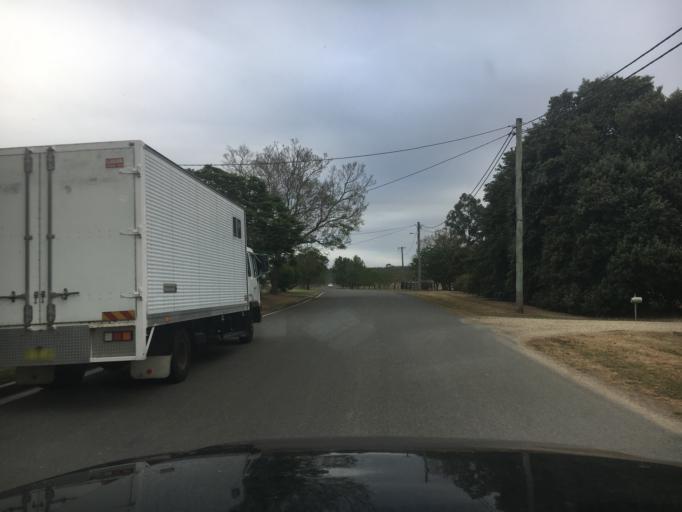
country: AU
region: New South Wales
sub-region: Singleton
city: Singleton
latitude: -32.5663
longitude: 151.1887
